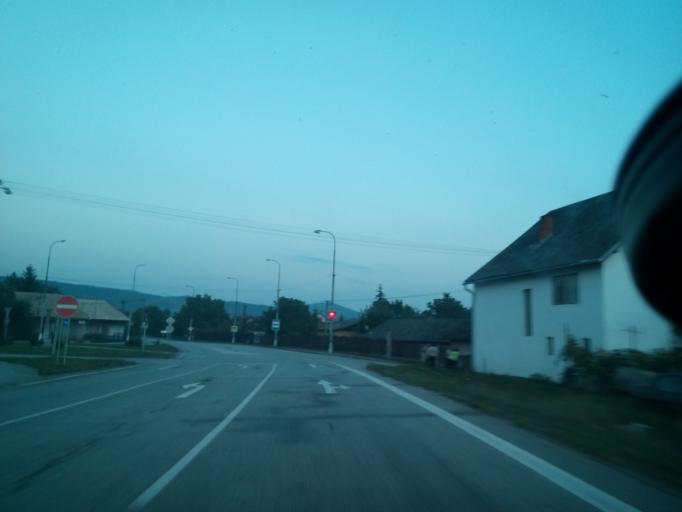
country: SK
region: Kosicky
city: Roznava
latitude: 48.7112
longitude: 20.4739
